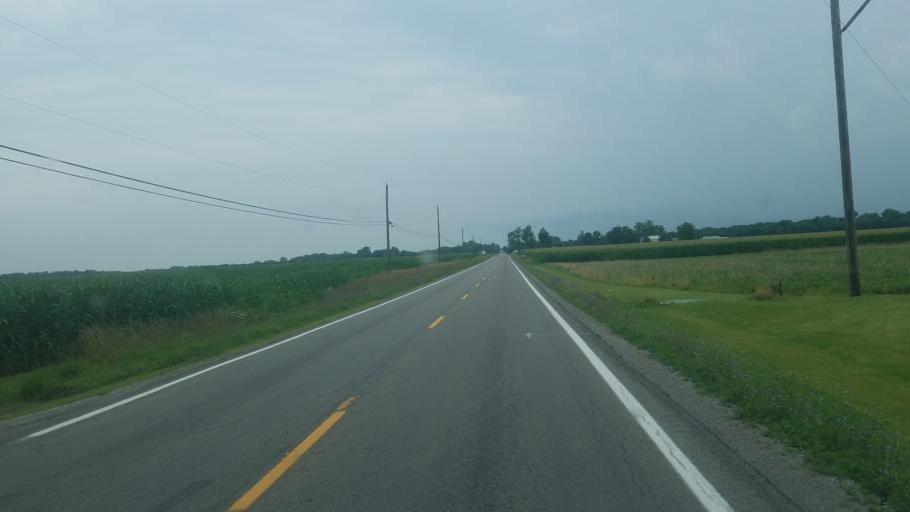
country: US
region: Ohio
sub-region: Hardin County
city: Kenton
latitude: 40.6301
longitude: -83.6361
